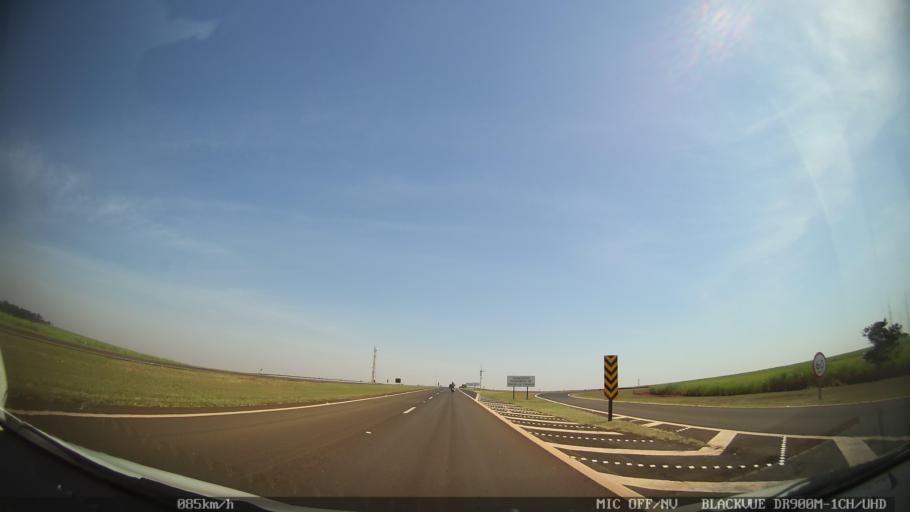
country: BR
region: Sao Paulo
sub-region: Ribeirao Preto
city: Ribeirao Preto
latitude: -21.1664
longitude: -47.8965
